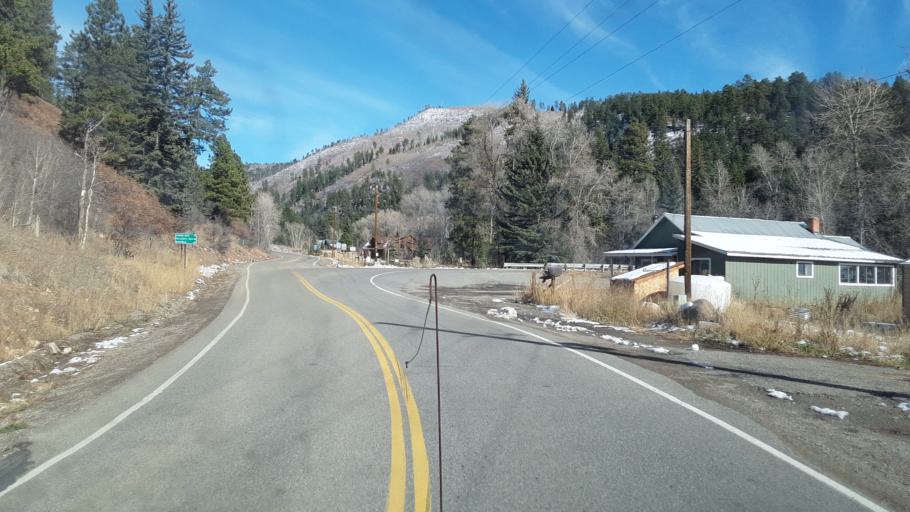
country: US
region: Colorado
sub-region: La Plata County
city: Bayfield
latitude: 37.3604
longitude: -107.6718
